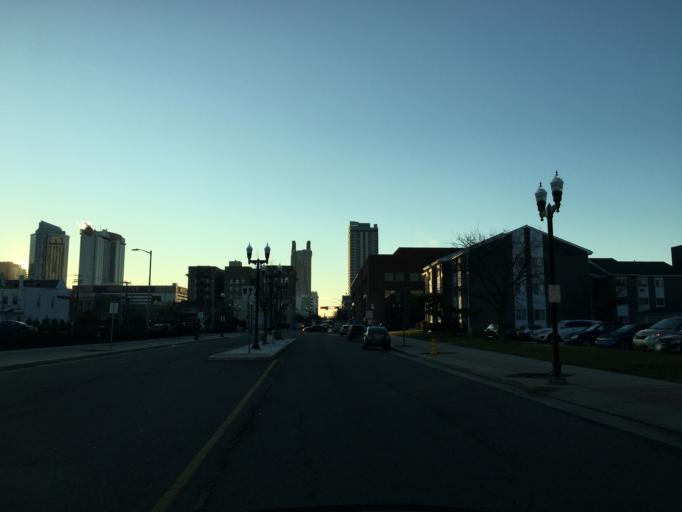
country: US
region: New Jersey
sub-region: Atlantic County
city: Atlantic City
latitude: 39.3656
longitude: -74.4272
